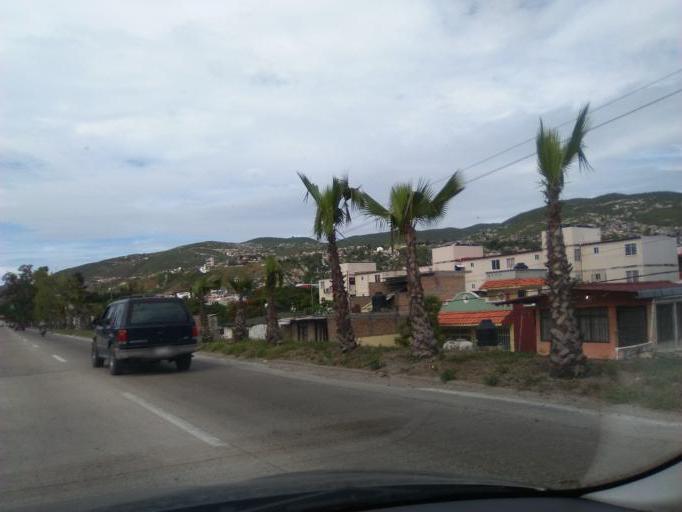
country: MX
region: Guerrero
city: Chilpancingo de los Bravos
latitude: 17.5555
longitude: -99.5093
